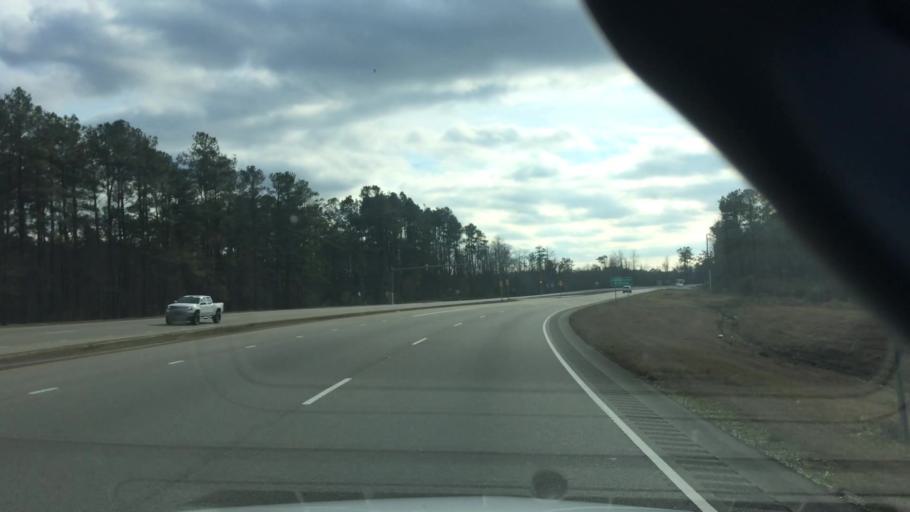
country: US
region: North Carolina
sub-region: Brunswick County
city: Bolivia
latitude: 34.1386
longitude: -78.0938
